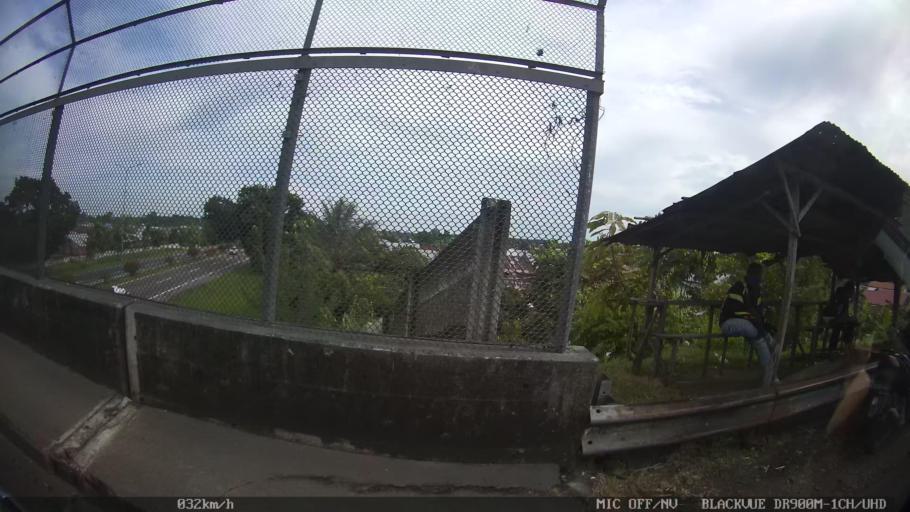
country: ID
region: North Sumatra
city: Medan
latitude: 3.6214
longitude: 98.7202
